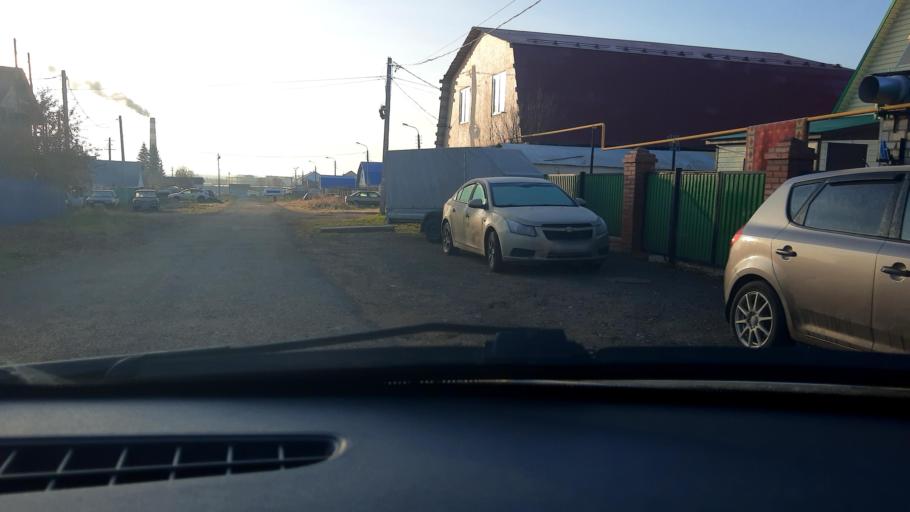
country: RU
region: Bashkortostan
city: Avdon
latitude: 54.6927
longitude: 55.8006
